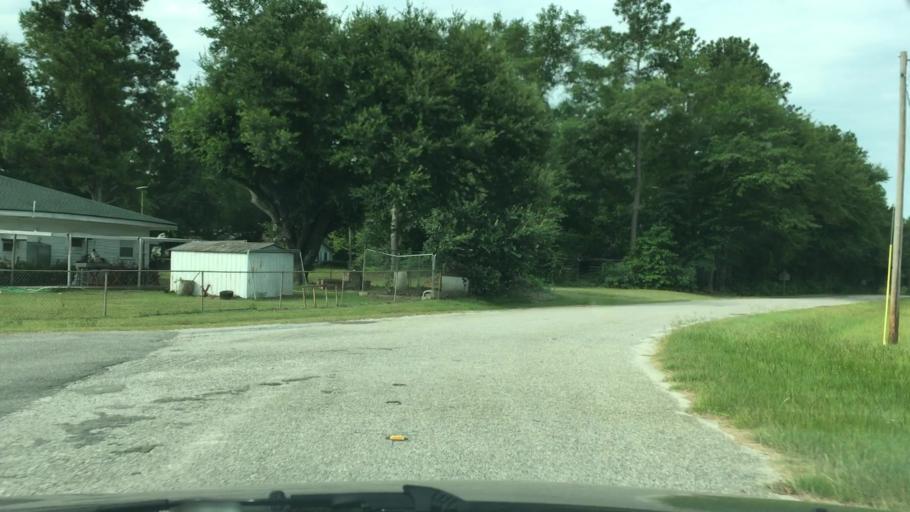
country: US
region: South Carolina
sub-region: Barnwell County
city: Williston
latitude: 33.6580
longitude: -81.3674
